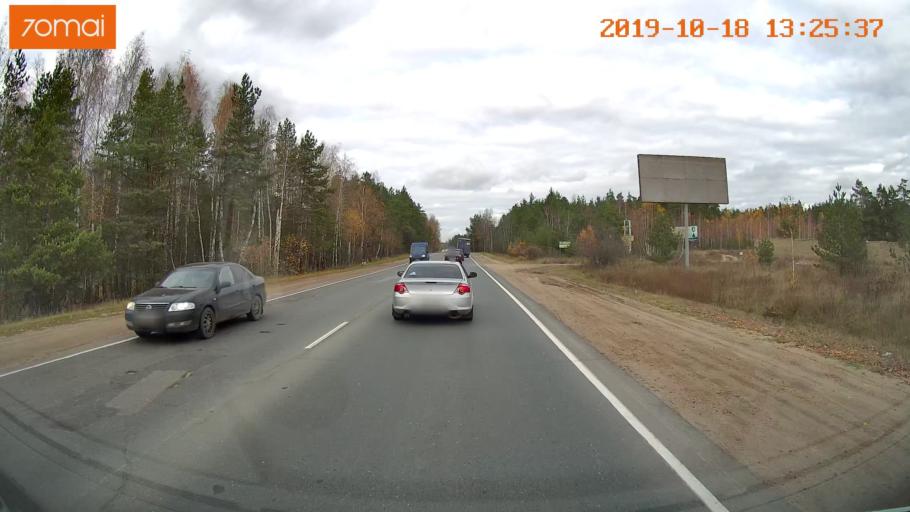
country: RU
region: Rjazan
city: Polyany
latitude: 54.7447
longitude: 39.8404
